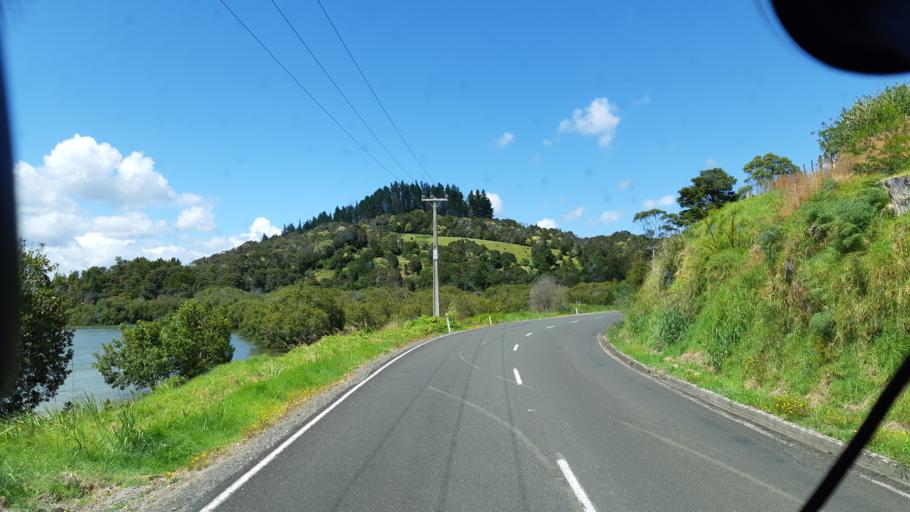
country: NZ
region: Northland
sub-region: Far North District
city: Taipa
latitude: -35.2742
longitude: 173.5214
